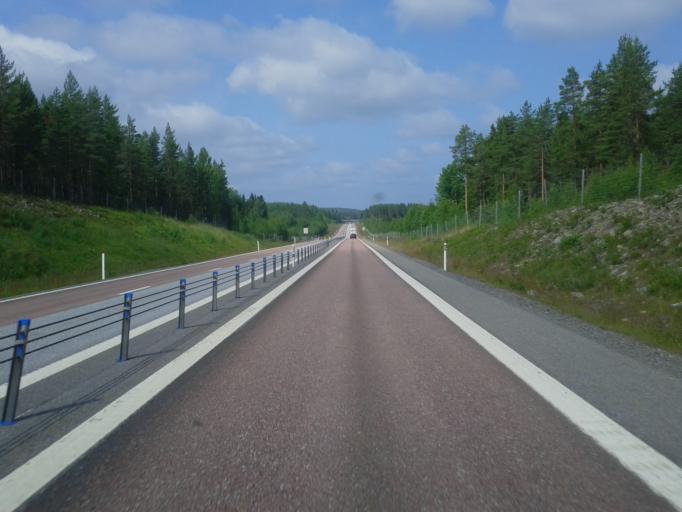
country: SE
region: Vaesterbotten
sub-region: Skelleftea Kommun
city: Soedra Bergsbyn
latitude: 64.6910
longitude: 21.0374
